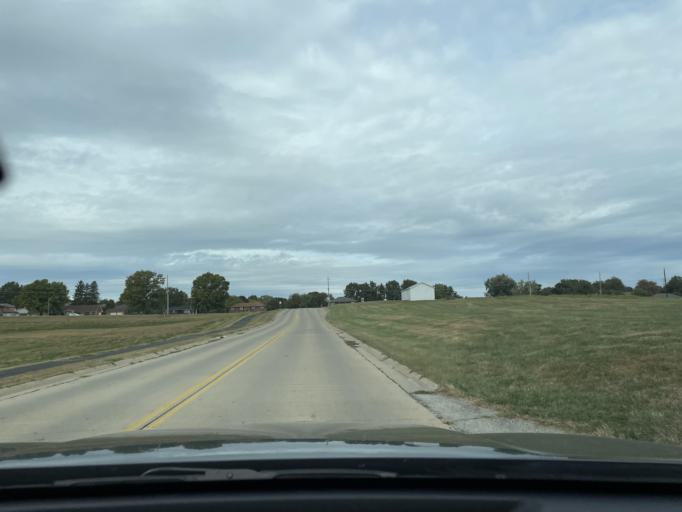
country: US
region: Missouri
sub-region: Buchanan County
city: Saint Joseph
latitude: 39.7677
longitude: -94.7811
